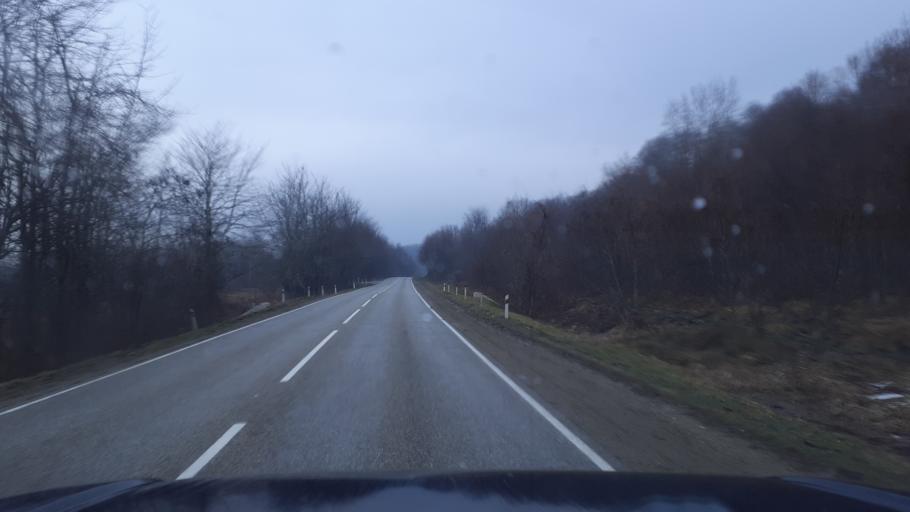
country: RU
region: Krasnodarskiy
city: Neftegorsk
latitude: 44.3138
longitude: 39.8326
